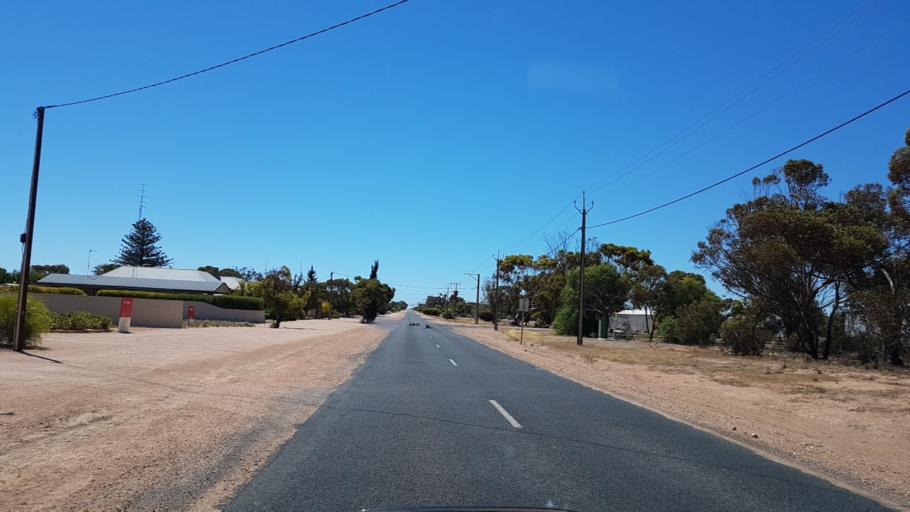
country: AU
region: South Australia
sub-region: Copper Coast
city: Wallaroo
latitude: -34.0603
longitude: 137.5930
